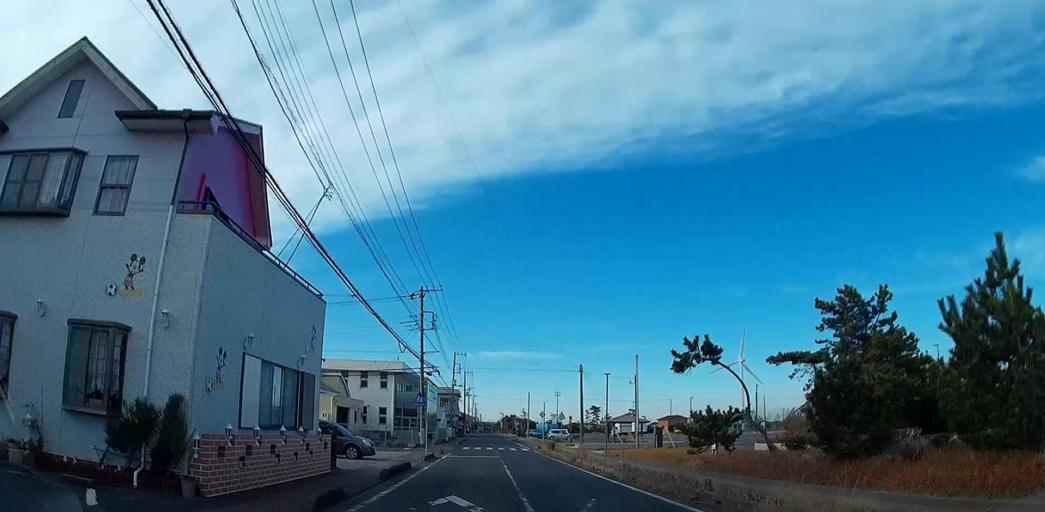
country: JP
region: Chiba
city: Hasaki
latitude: 35.7482
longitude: 140.8333
